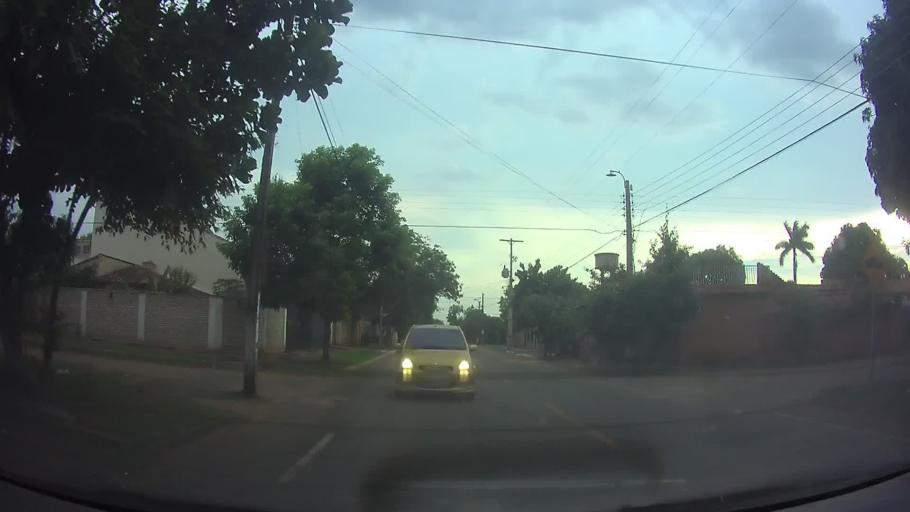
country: PY
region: Central
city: San Lorenzo
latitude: -25.2728
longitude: -57.4771
